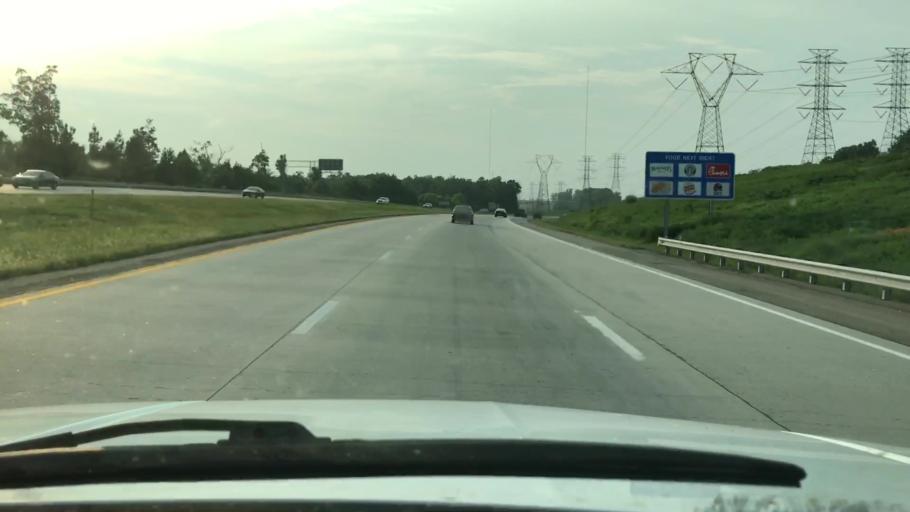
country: US
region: Virginia
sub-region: Chesterfield County
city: Brandermill
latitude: 37.4914
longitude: -77.6785
